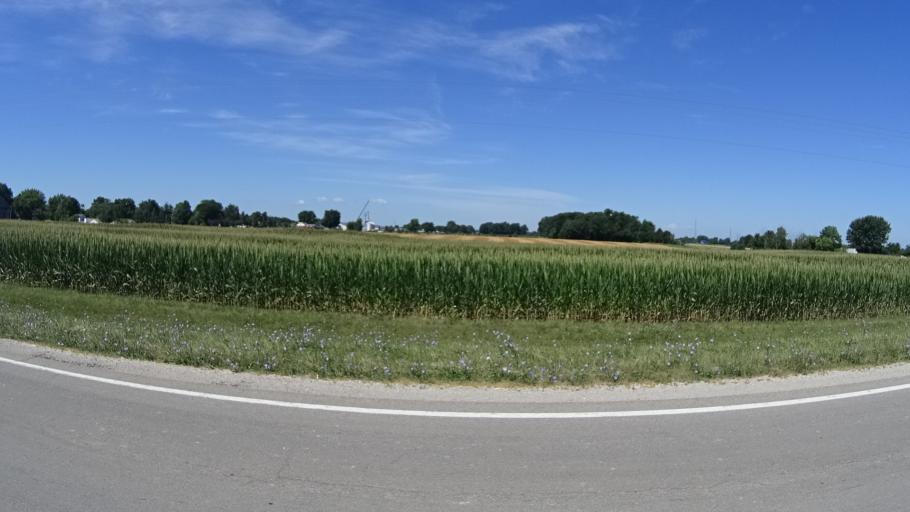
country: US
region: Ohio
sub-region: Erie County
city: Sandusky
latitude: 41.3983
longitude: -82.7068
